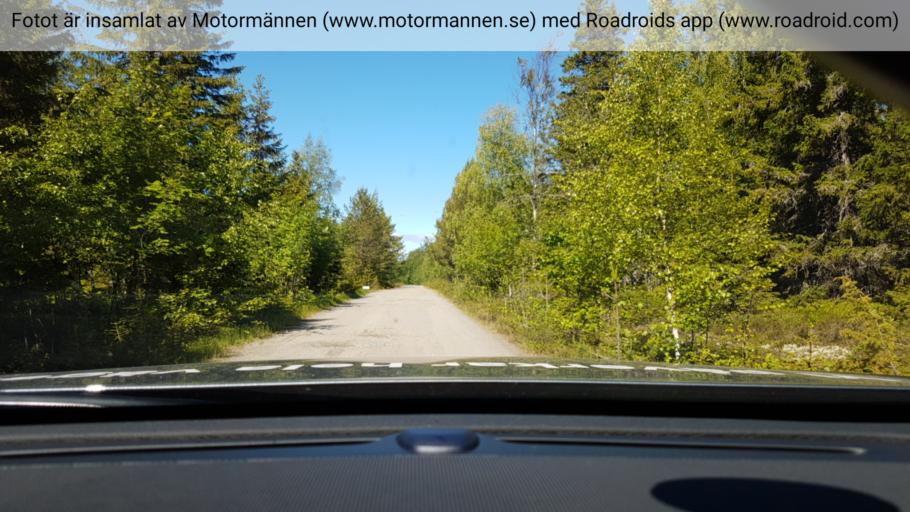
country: SE
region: Vaesterbotten
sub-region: Skelleftea Kommun
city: Skelleftehamn
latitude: 64.4704
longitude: 21.5806
